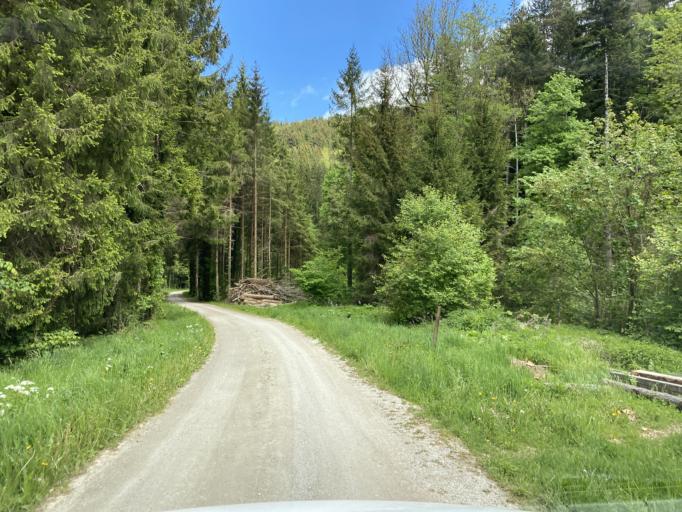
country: AT
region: Styria
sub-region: Politischer Bezirk Weiz
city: Koglhof
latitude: 47.3117
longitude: 15.6908
